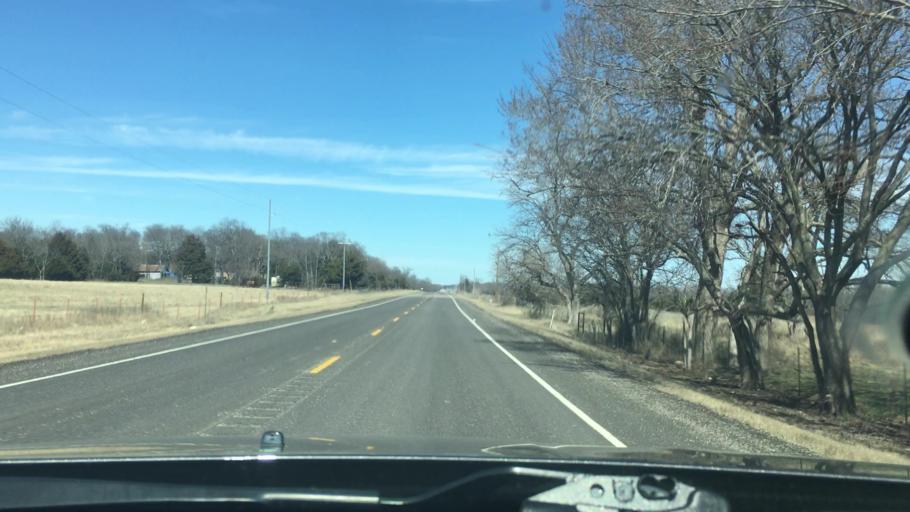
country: US
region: Oklahoma
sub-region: Murray County
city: Sulphur
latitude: 34.3528
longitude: -96.9508
